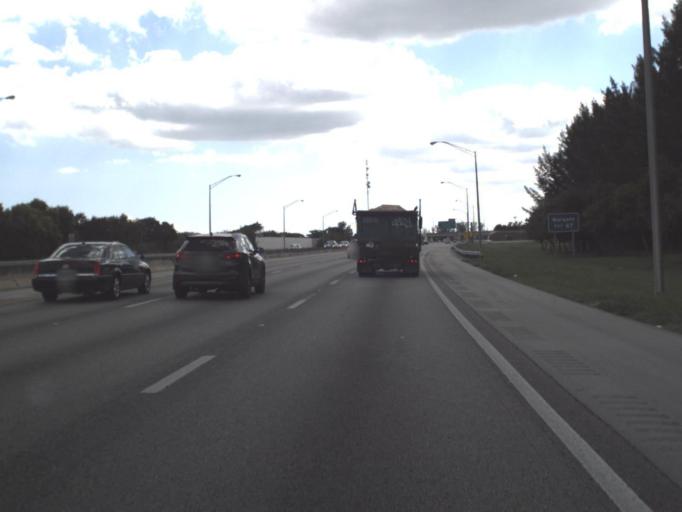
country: US
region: Florida
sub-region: Broward County
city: Coconut Creek
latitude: 26.2562
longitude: -80.1667
